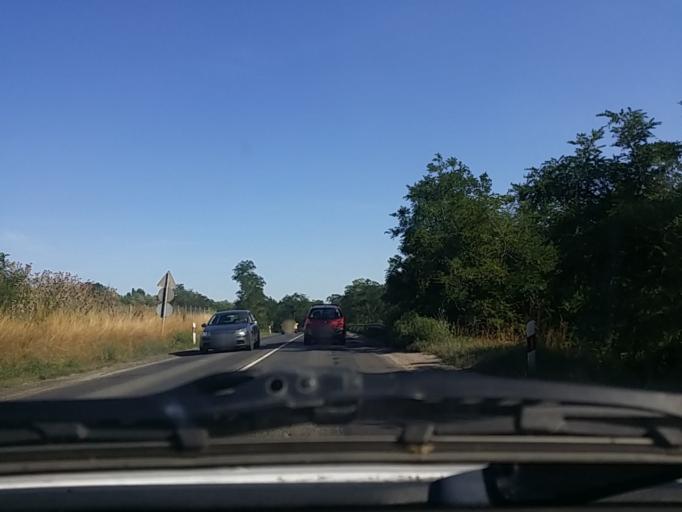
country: HU
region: Pest
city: Pilisborosjeno
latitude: 47.5952
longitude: 18.9793
